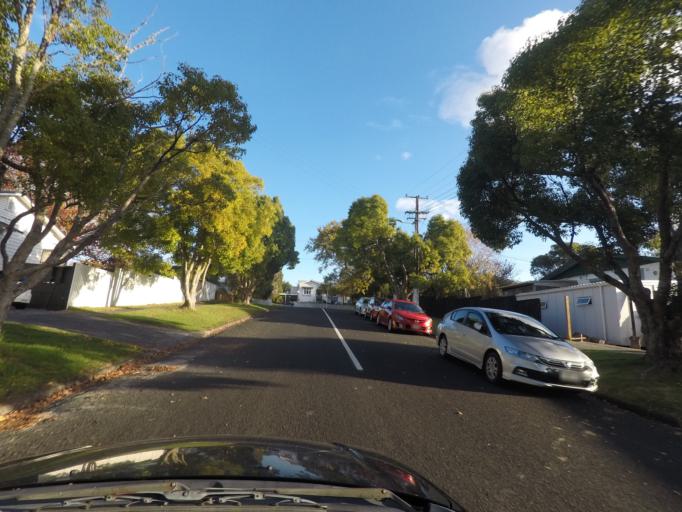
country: NZ
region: Auckland
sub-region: Auckland
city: Waitakere
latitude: -36.9030
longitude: 174.6720
